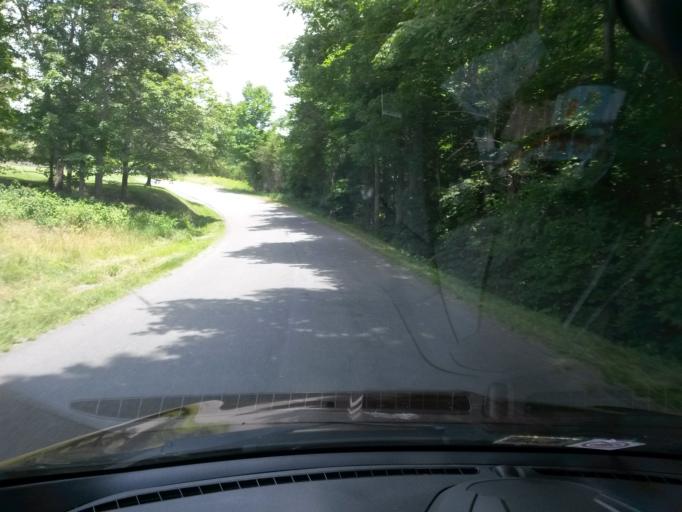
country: US
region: West Virginia
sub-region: Monroe County
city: Union
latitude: 37.5220
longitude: -80.5562
